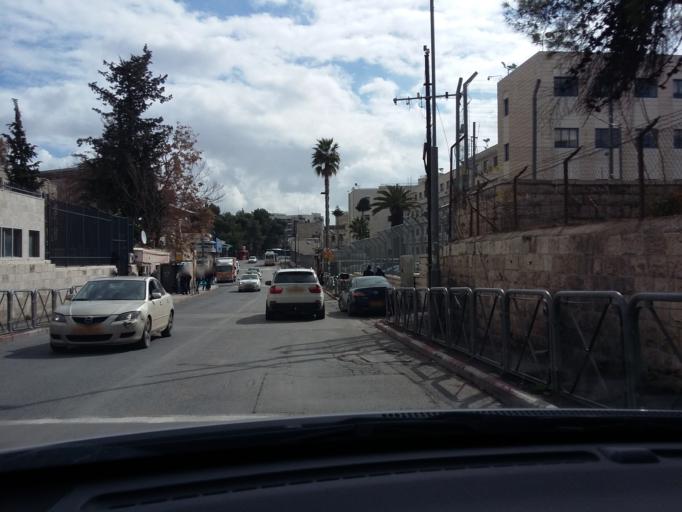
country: PS
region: West Bank
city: East Jerusalem
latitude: 31.7877
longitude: 35.2297
